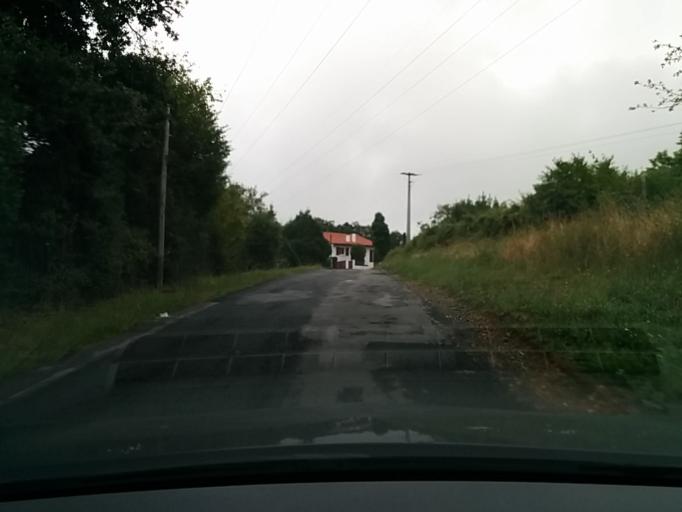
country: FR
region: Aquitaine
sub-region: Departement des Pyrenees-Atlantiques
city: Saint-Jean-de-Luz
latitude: 43.3935
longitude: -1.6361
